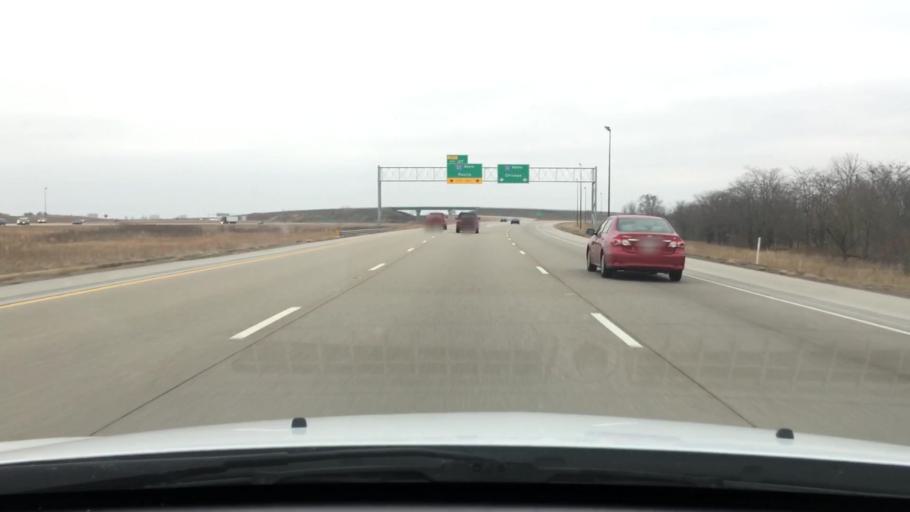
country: US
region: Illinois
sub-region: Logan County
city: Lincoln
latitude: 40.1713
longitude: -89.4172
